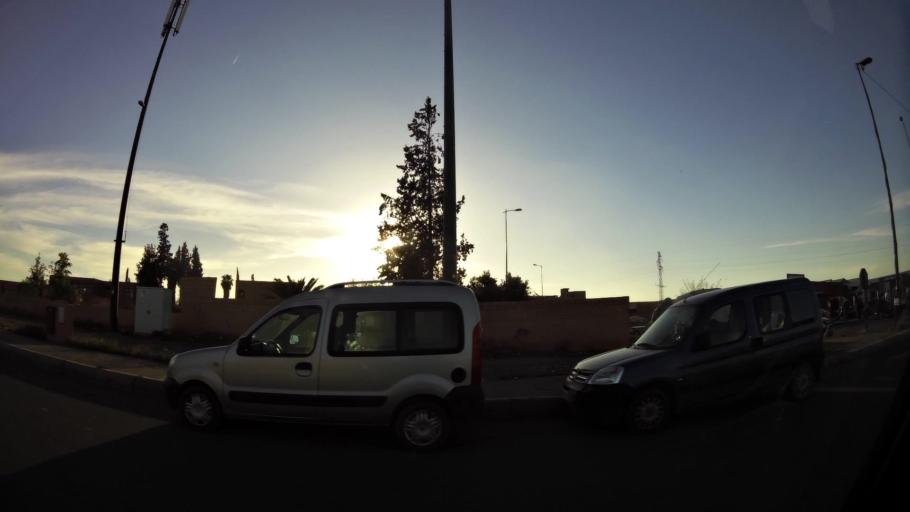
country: MA
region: Marrakech-Tensift-Al Haouz
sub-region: Marrakech
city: Marrakesh
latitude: 31.6222
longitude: -8.0439
